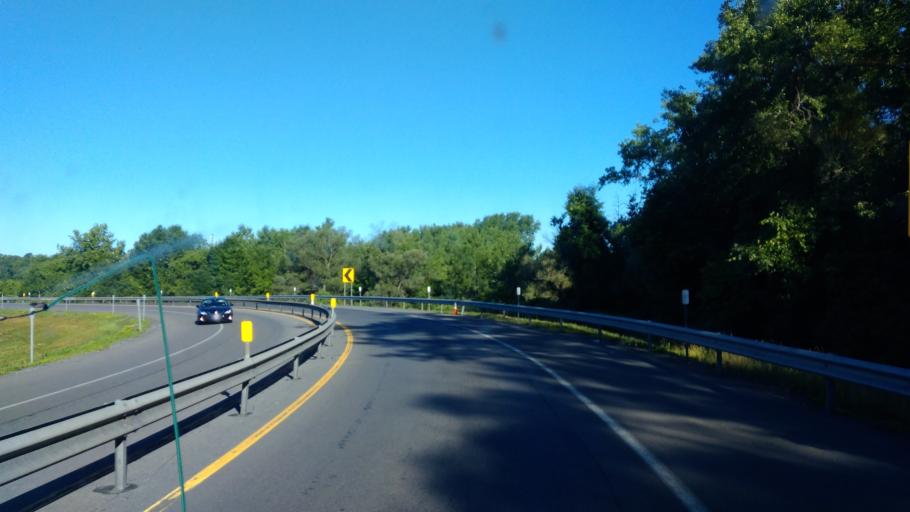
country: US
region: New York
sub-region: Ontario County
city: Phelps
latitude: 42.9569
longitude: -76.9822
